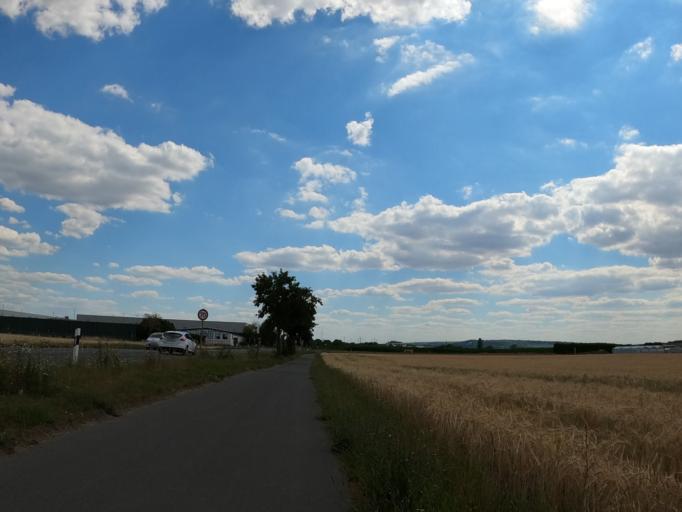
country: DE
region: Hesse
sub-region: Regierungsbezirk Darmstadt
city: Trebur
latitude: 49.8960
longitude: 8.4014
